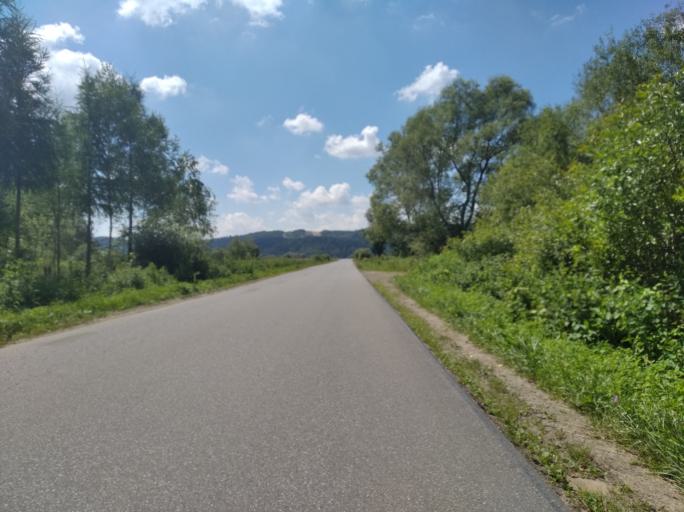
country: PL
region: Subcarpathian Voivodeship
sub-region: Powiat brzozowski
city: Dydnia
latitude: 49.7050
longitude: 22.2093
